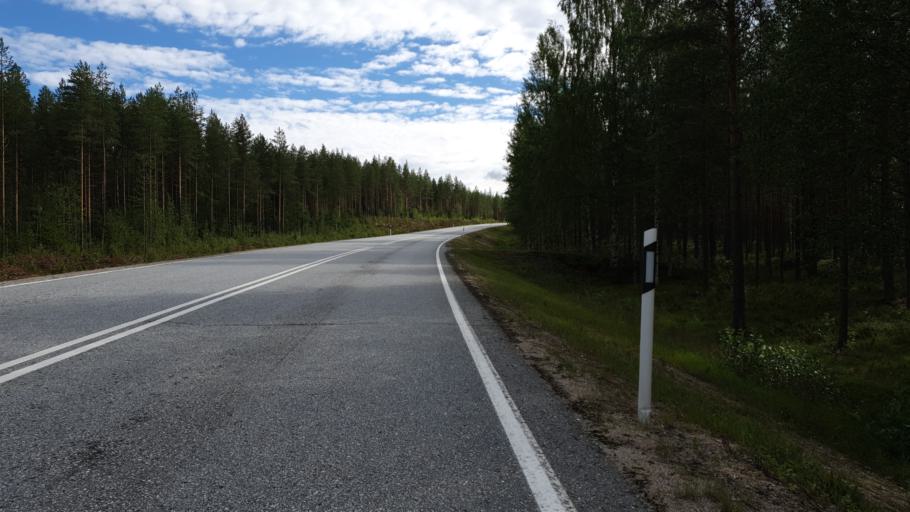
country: FI
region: Kainuu
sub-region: Kehys-Kainuu
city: Kuhmo
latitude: 64.4900
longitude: 29.8158
